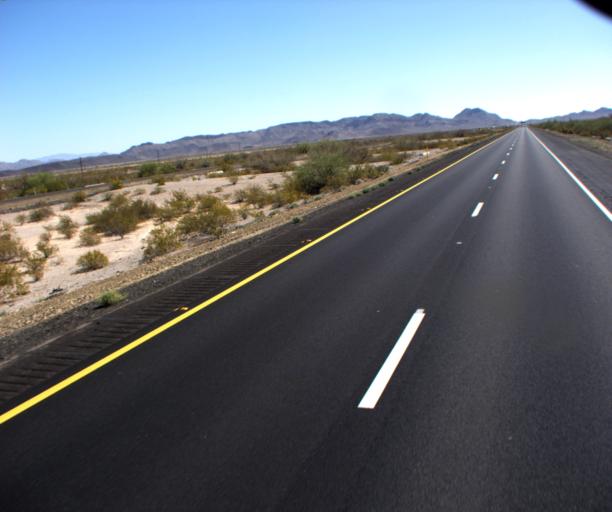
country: US
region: Arizona
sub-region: La Paz County
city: Salome
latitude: 33.6227
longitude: -113.7136
